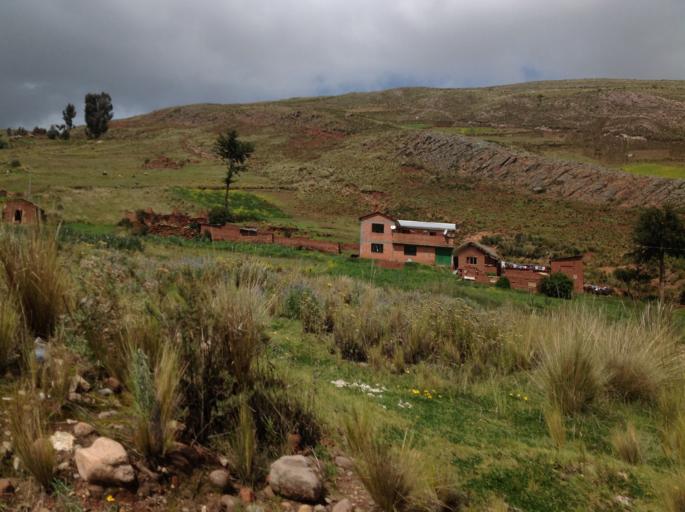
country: BO
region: La Paz
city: Yumani
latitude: -15.7735
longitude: -69.0015
